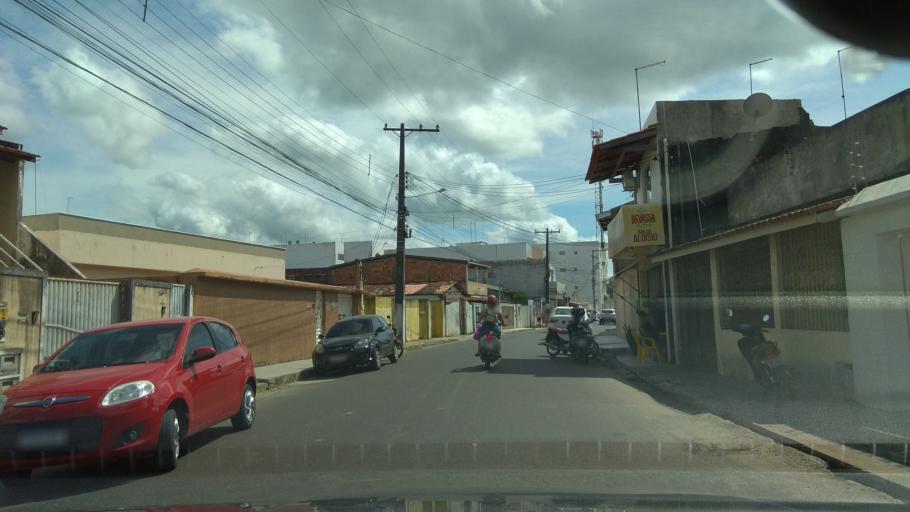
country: BR
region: Bahia
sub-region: Santo Antonio De Jesus
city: Santo Antonio de Jesus
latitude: -12.9753
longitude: -39.2678
